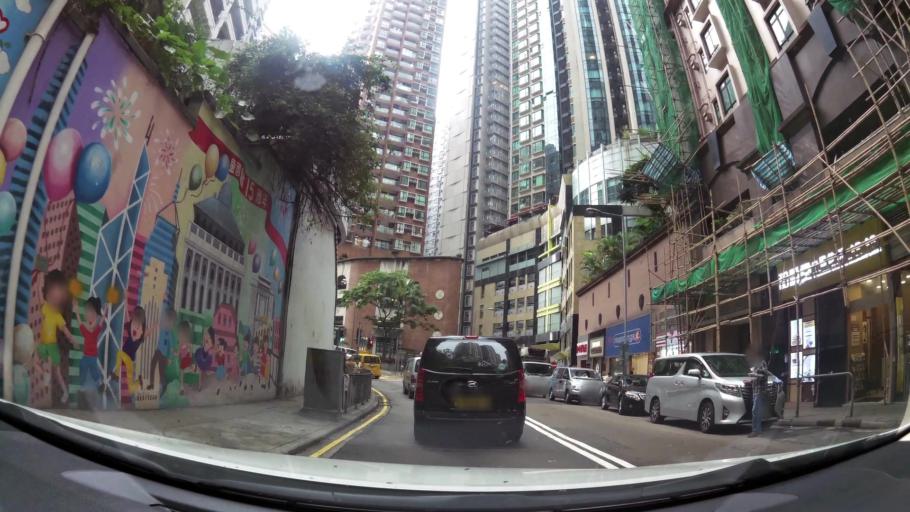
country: HK
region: Central and Western
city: Central
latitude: 22.2795
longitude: 114.1516
